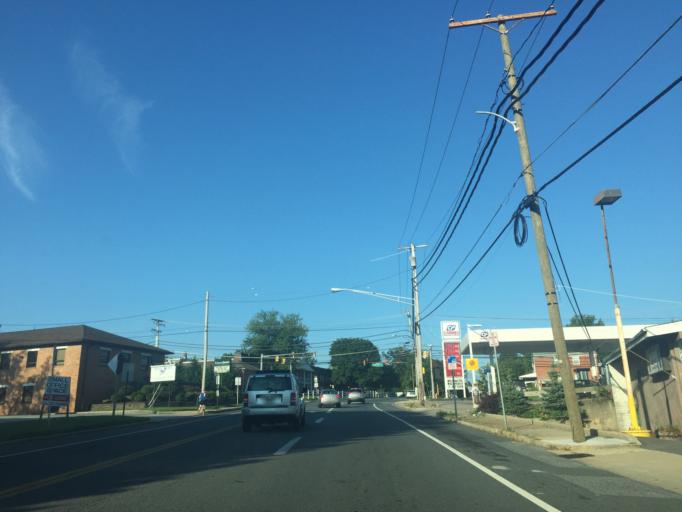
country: US
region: Maryland
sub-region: Baltimore County
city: Catonsville
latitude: 39.2778
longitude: -76.7323
